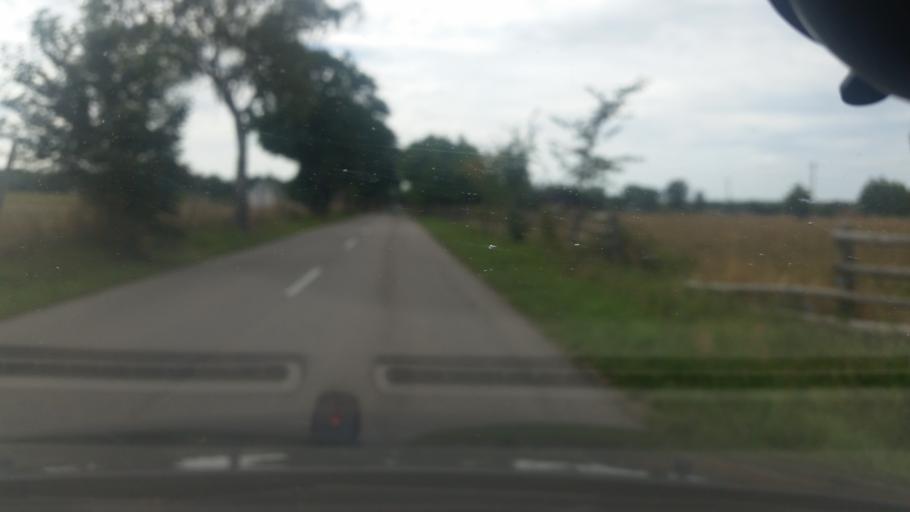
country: PL
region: Pomeranian Voivodeship
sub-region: Powiat leborski
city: Leba
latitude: 54.7337
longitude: 17.6293
